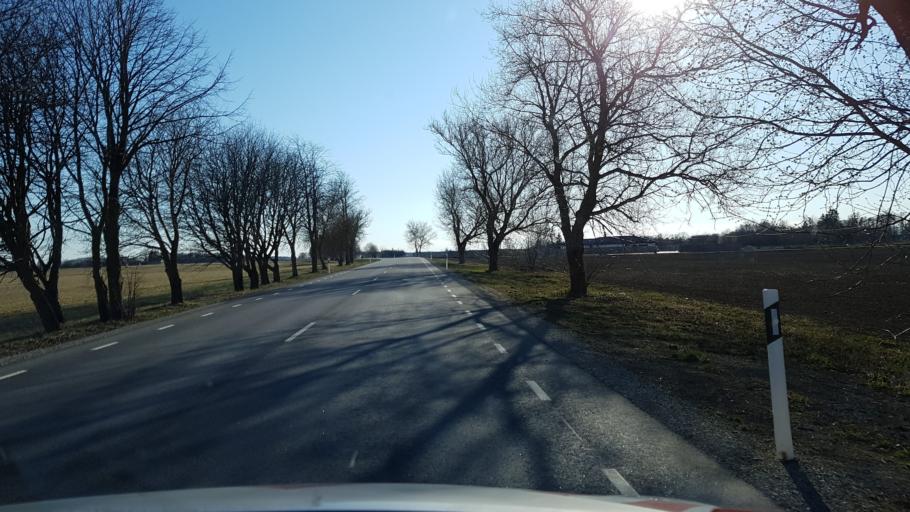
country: EE
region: Ida-Virumaa
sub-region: Johvi vald
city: Johvi
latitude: 59.3487
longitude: 27.3738
